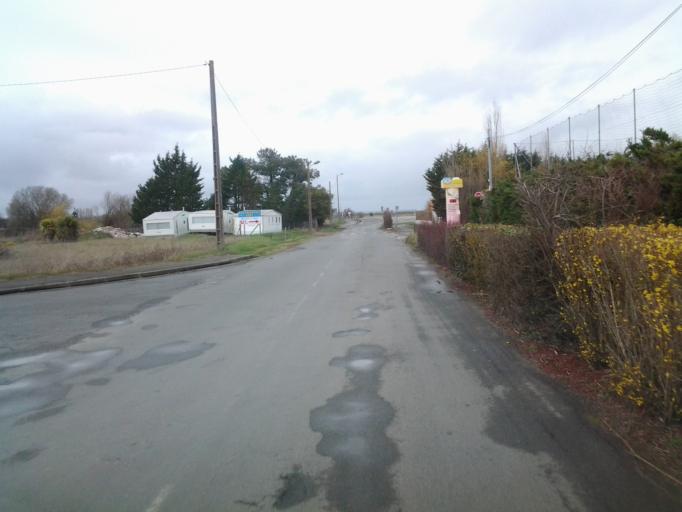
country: FR
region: Pays de la Loire
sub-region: Departement de la Vendee
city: La Tranche-sur-Mer
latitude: 46.3605
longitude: -1.4516
